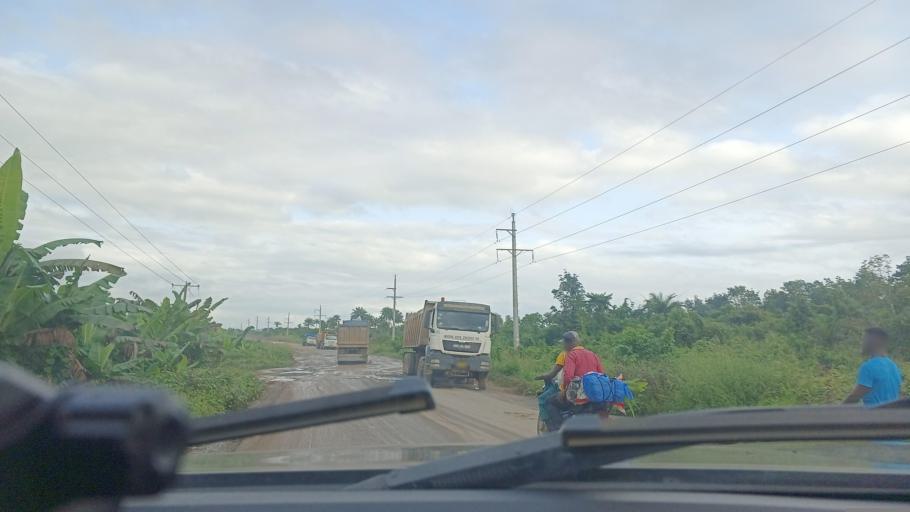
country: LR
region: Montserrado
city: Monrovia
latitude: 6.5733
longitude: -10.8817
